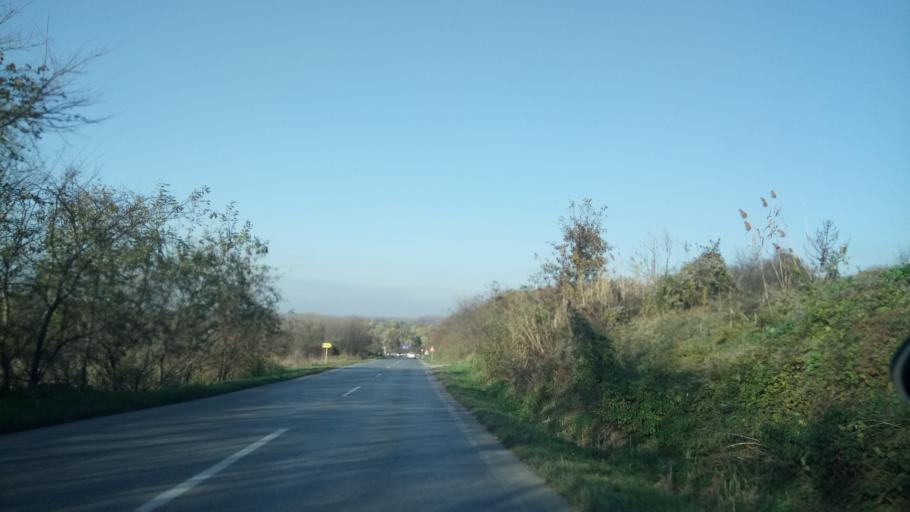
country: RS
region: Autonomna Pokrajina Vojvodina
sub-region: Juznobacki Okrug
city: Sremski Karlovci
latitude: 45.1883
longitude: 19.9534
